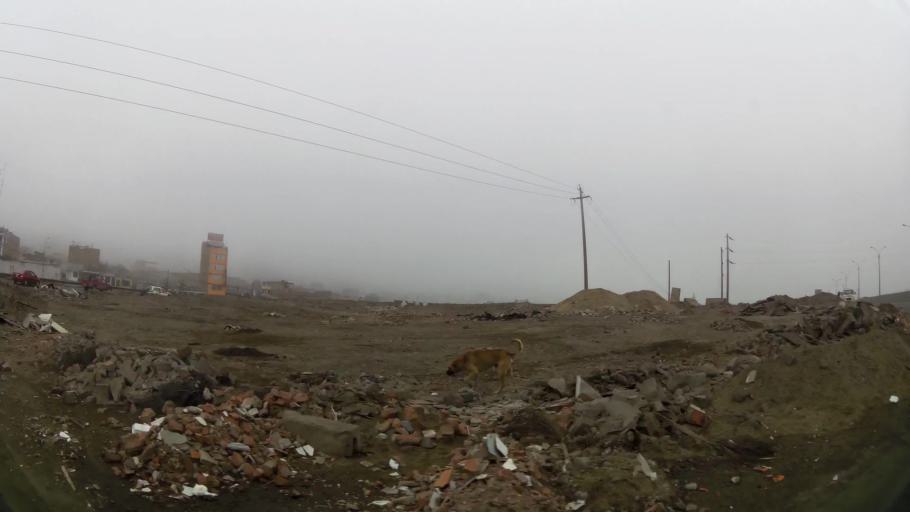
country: PE
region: Lima
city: Ventanilla
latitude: -11.8352
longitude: -77.1109
